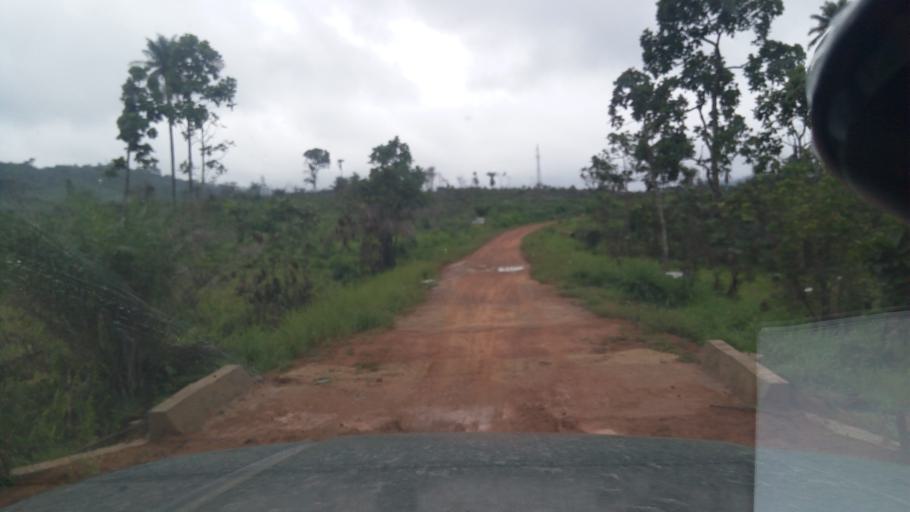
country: SL
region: Eastern Province
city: Panguma
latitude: 8.1346
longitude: -11.1831
